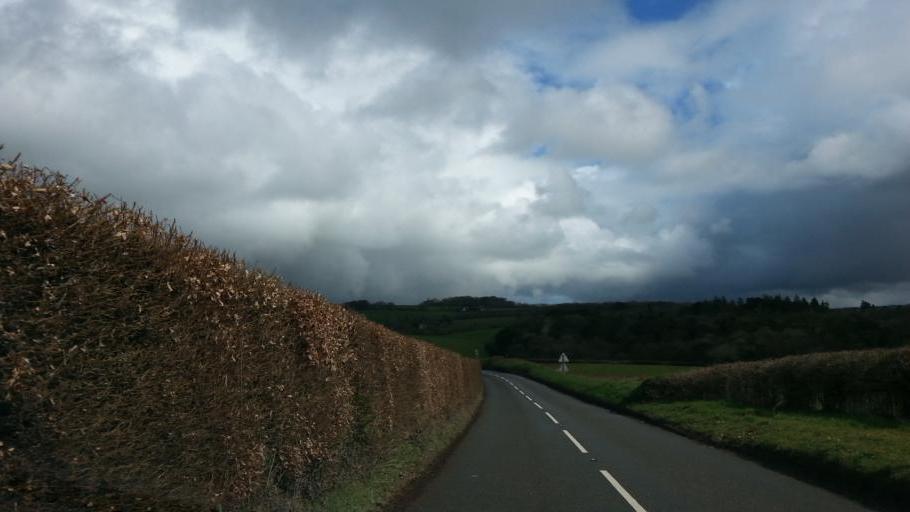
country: GB
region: England
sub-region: Devon
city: Barnstaple
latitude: 51.1231
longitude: -4.0149
